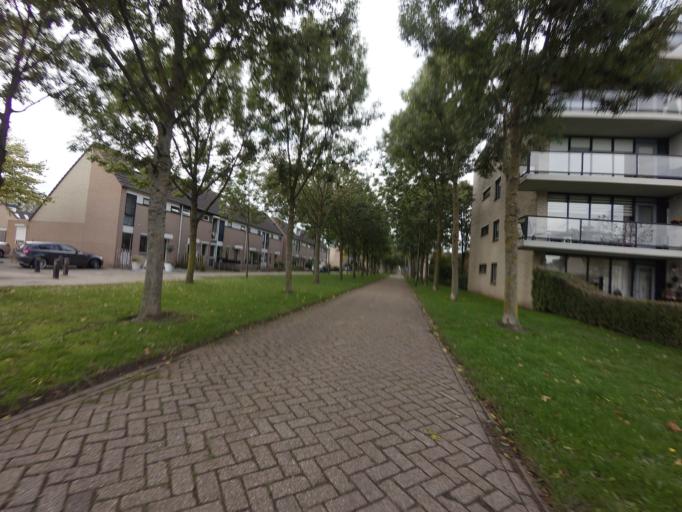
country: NL
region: North Brabant
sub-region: Gemeente Breda
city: Hoge Vucht
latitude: 51.6240
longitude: 4.7505
